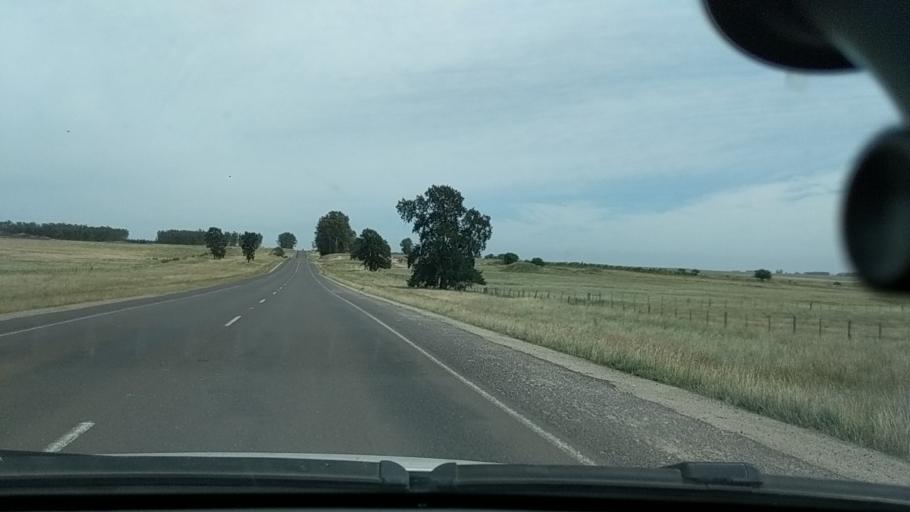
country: UY
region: Durazno
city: Durazno
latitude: -33.4686
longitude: -56.4561
